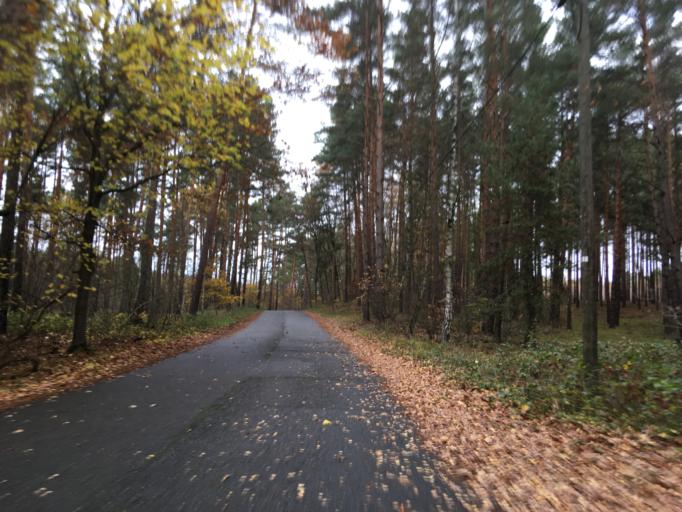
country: DE
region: Brandenburg
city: Mixdorf
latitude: 52.0963
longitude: 14.4337
